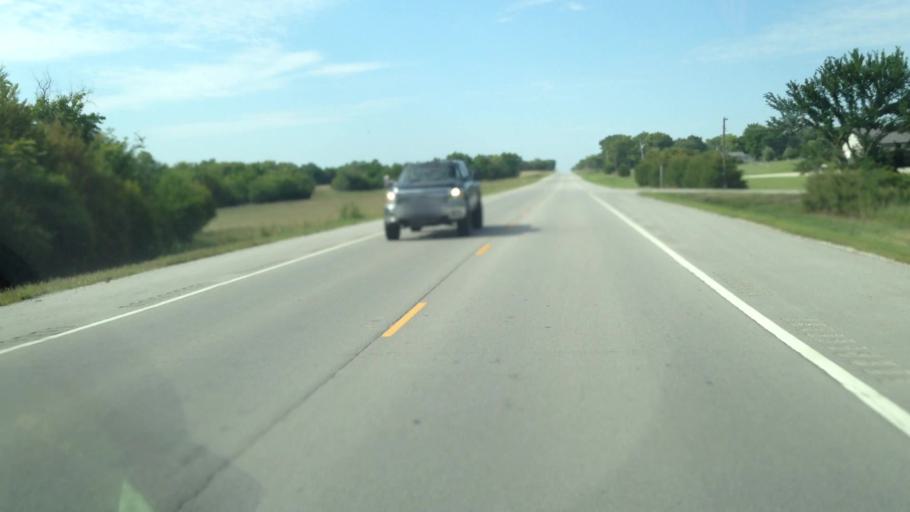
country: US
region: Kansas
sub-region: Labette County
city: Parsons
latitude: 37.2953
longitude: -95.2675
